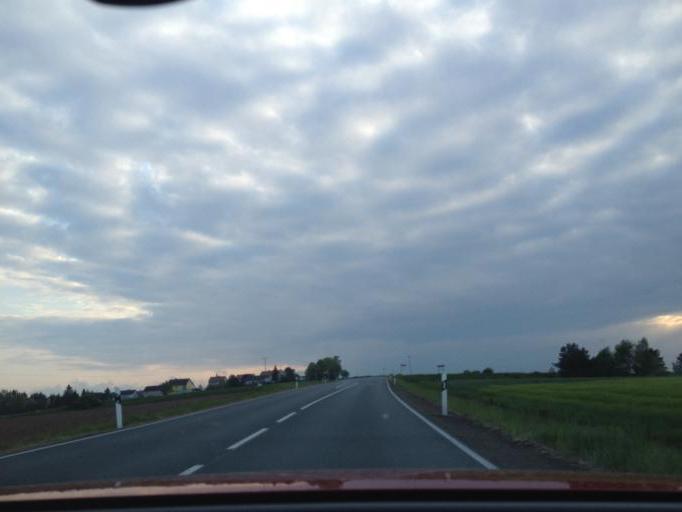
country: DE
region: Bavaria
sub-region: Upper Palatinate
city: Kohlberg
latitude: 49.6019
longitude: 12.0305
